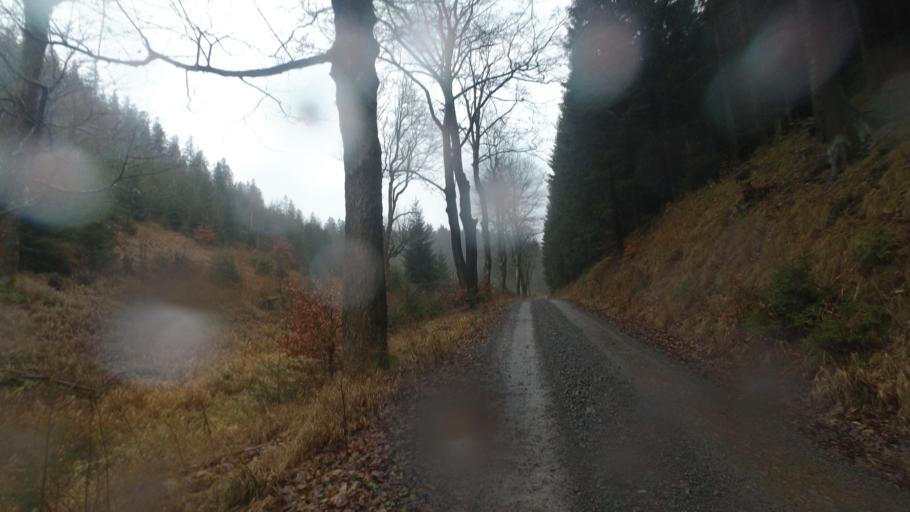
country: DE
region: Thuringia
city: Frankenhain
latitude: 50.7155
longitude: 10.7673
